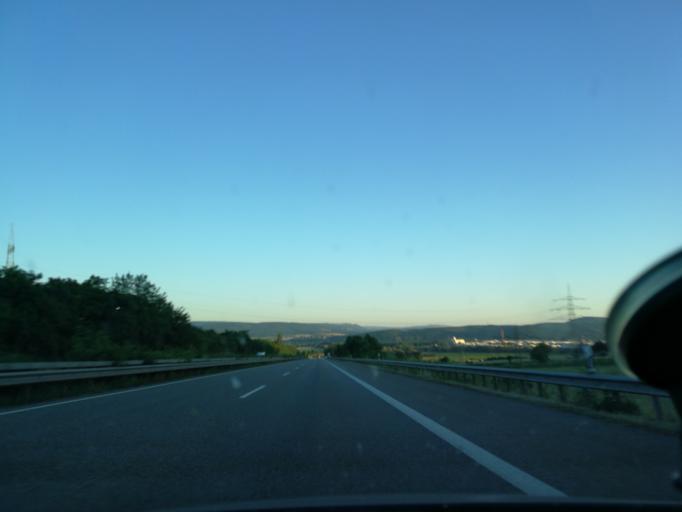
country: DE
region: Rheinland-Pfalz
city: Flussbach
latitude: 50.0021
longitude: 6.9294
